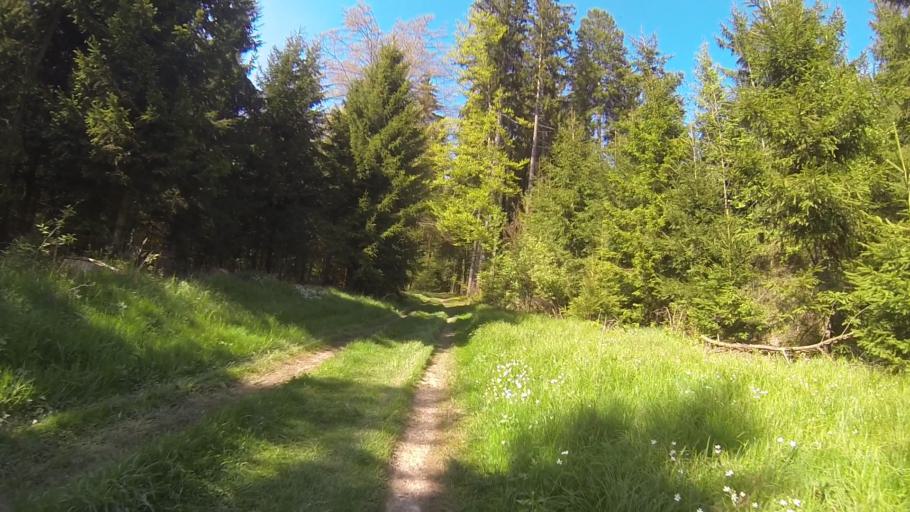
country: DE
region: Baden-Wuerttemberg
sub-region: Regierungsbezirk Stuttgart
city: Bartholoma
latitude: 48.7682
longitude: 10.0201
